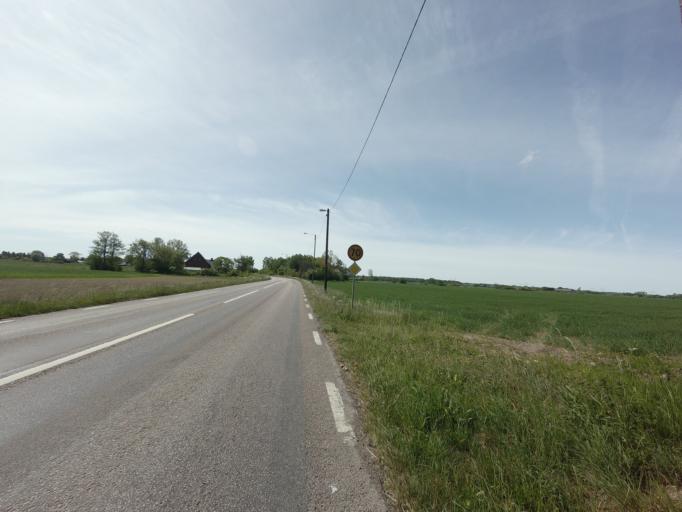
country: SE
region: Skane
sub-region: Helsingborg
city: Odakra
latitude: 56.1499
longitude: 12.6782
